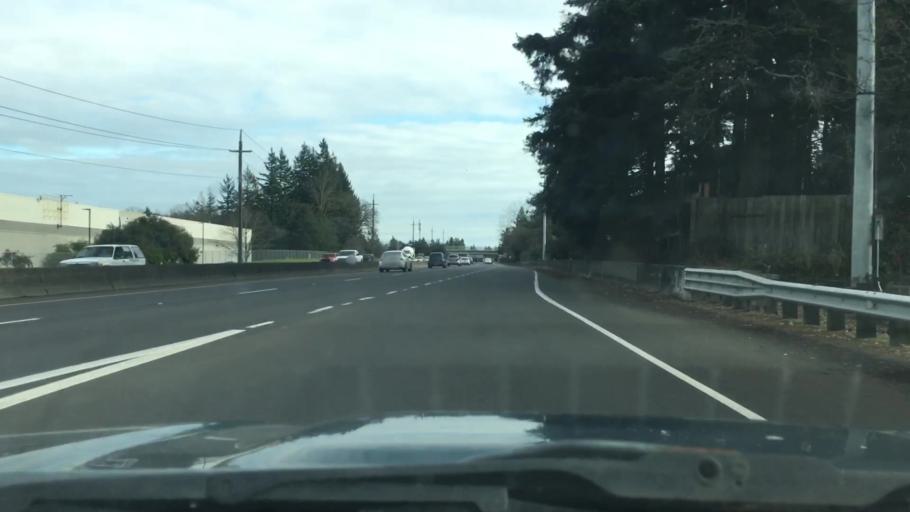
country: US
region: Oregon
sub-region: Lane County
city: Eugene
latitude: 44.0901
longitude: -123.0952
